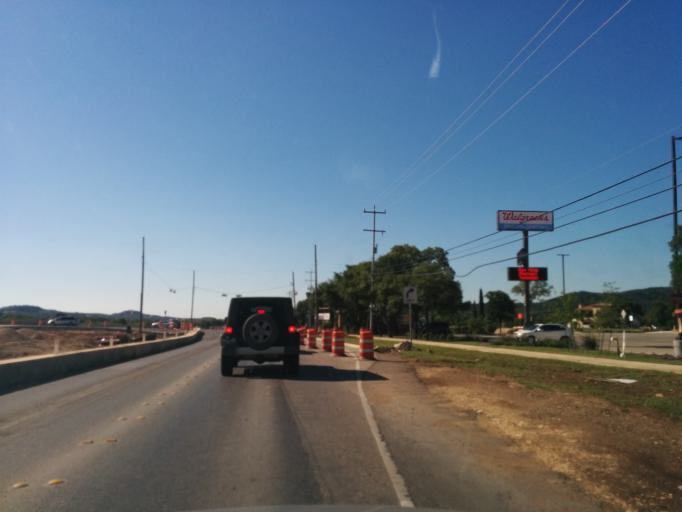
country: US
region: Texas
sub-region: Bexar County
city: Cross Mountain
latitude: 29.6766
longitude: -98.6372
